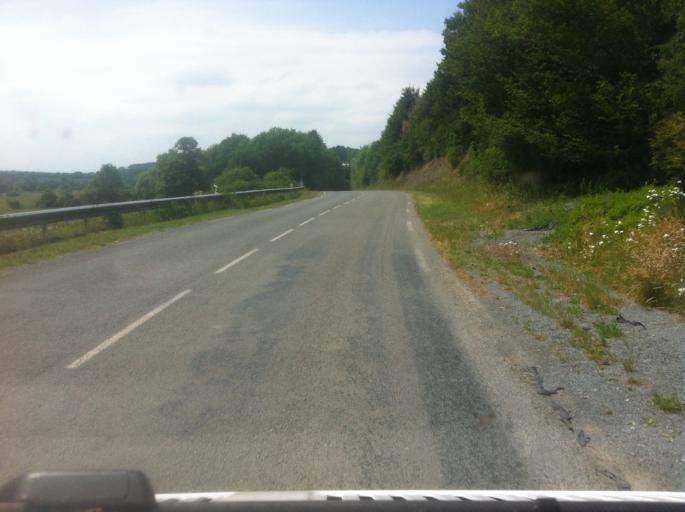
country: FR
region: Nord-Pas-de-Calais
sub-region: Departement du Nord
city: Trelon
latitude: 50.1209
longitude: 4.1709
